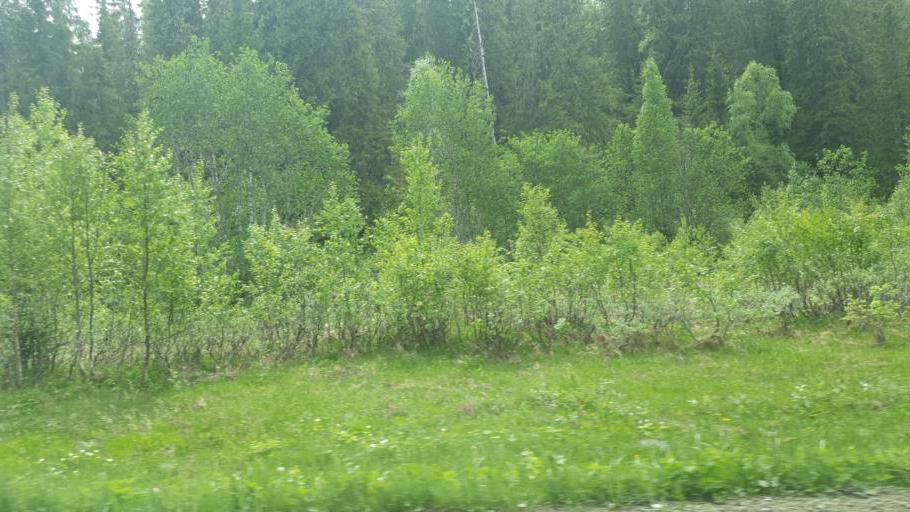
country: NO
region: Nord-Trondelag
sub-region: Leksvik
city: Leksvik
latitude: 63.6937
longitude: 10.4471
